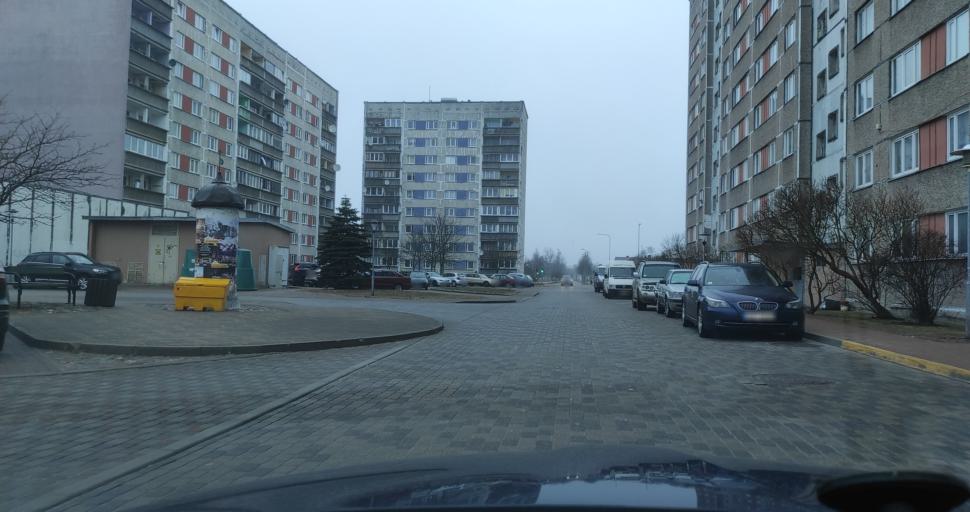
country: LV
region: Ventspils
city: Ventspils
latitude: 57.3828
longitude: 21.5494
